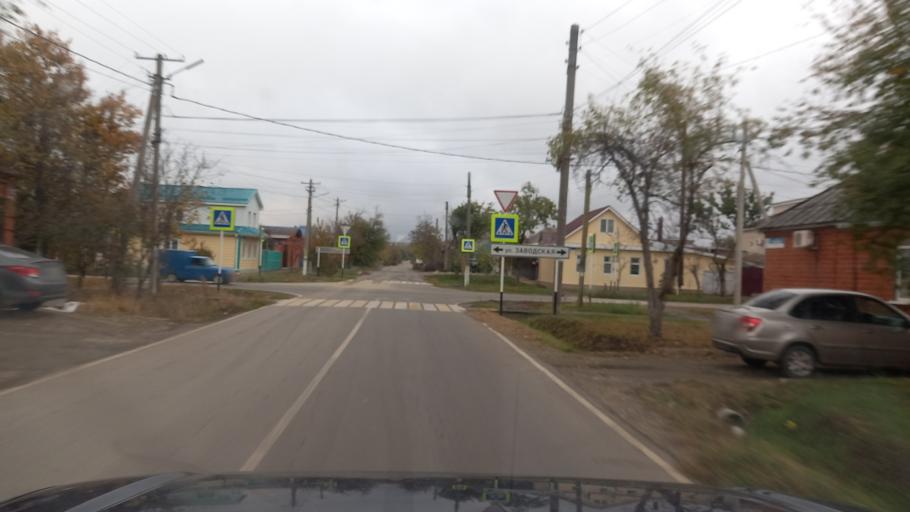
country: RU
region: Adygeya
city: Maykop
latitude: 44.6104
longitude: 40.1263
